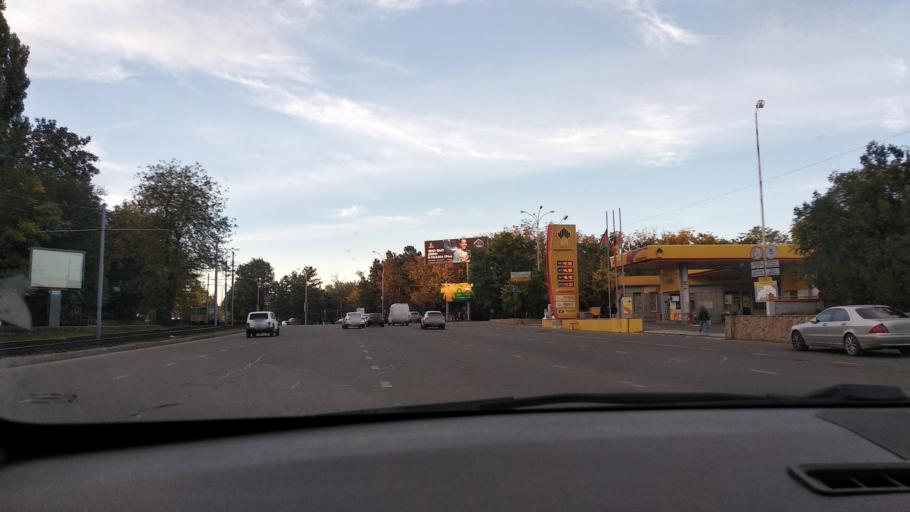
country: RU
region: Krasnodarskiy
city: Krasnodar
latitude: 45.0225
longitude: 38.9970
